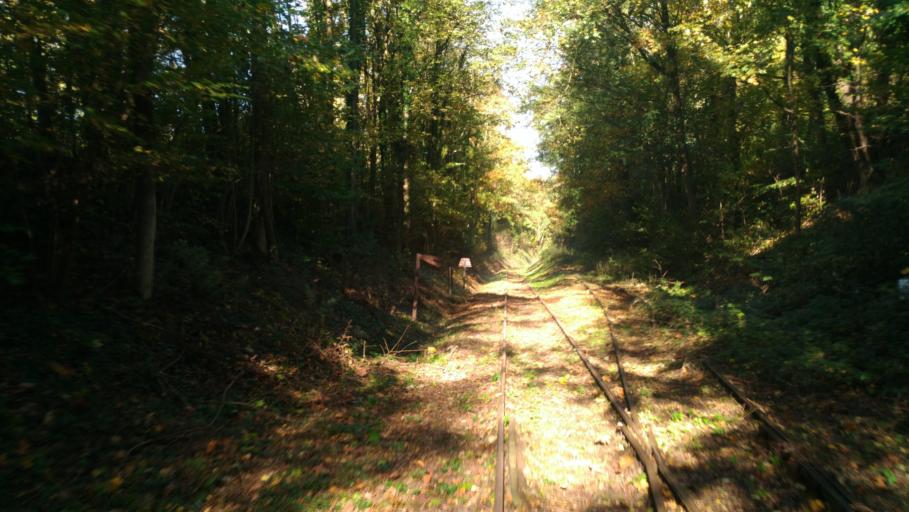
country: DE
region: Lower Saxony
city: Buchholz
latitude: 52.2168
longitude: 9.1200
